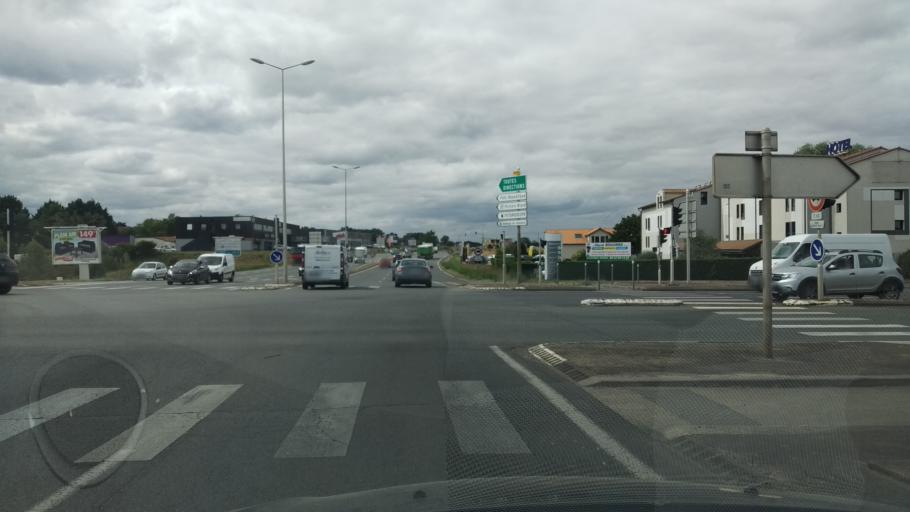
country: FR
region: Poitou-Charentes
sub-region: Departement de la Vienne
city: Biard
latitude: 46.5545
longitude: 0.3072
